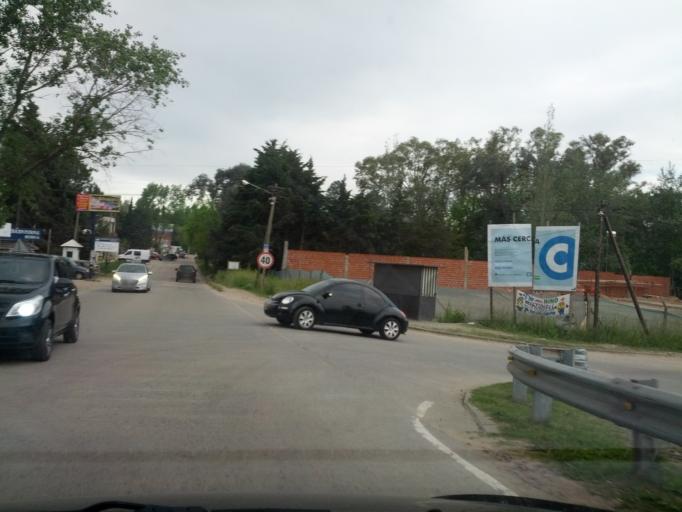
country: AR
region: Buenos Aires
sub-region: Partido de General Rodriguez
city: General Rodriguez
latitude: -34.6093
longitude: -58.8688
